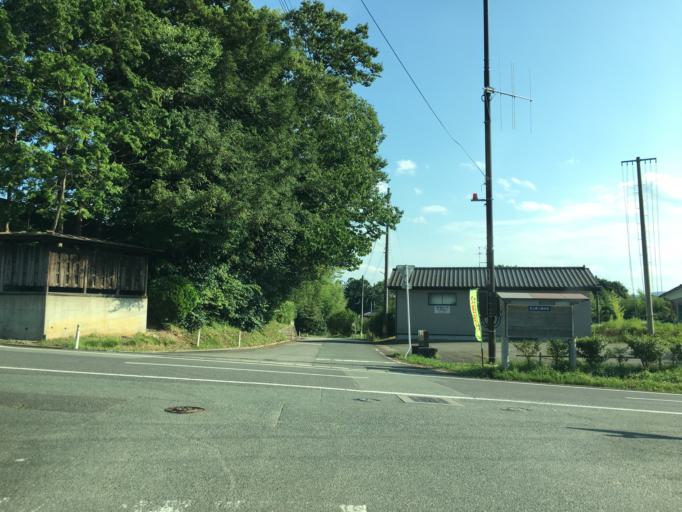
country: JP
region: Miyagi
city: Marumori
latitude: 37.8243
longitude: 140.9133
